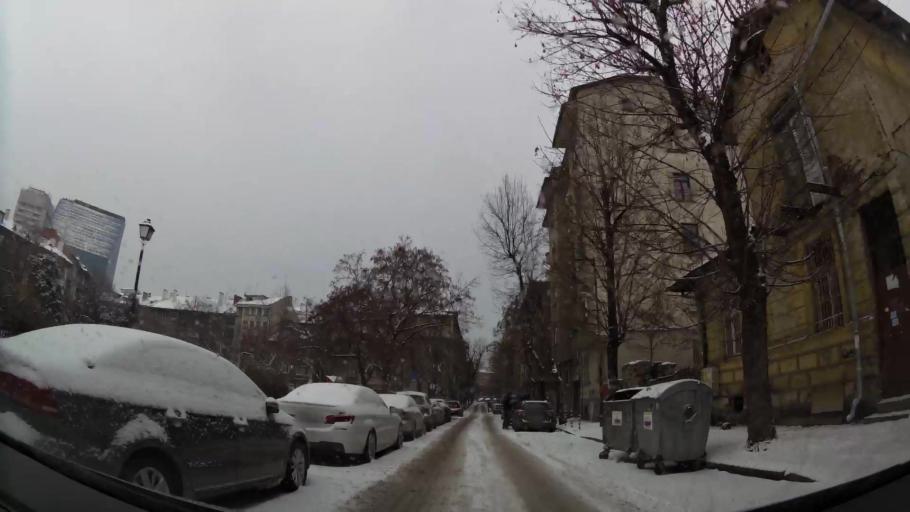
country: BG
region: Sofia-Capital
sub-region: Stolichna Obshtina
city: Sofia
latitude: 42.6952
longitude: 23.3128
